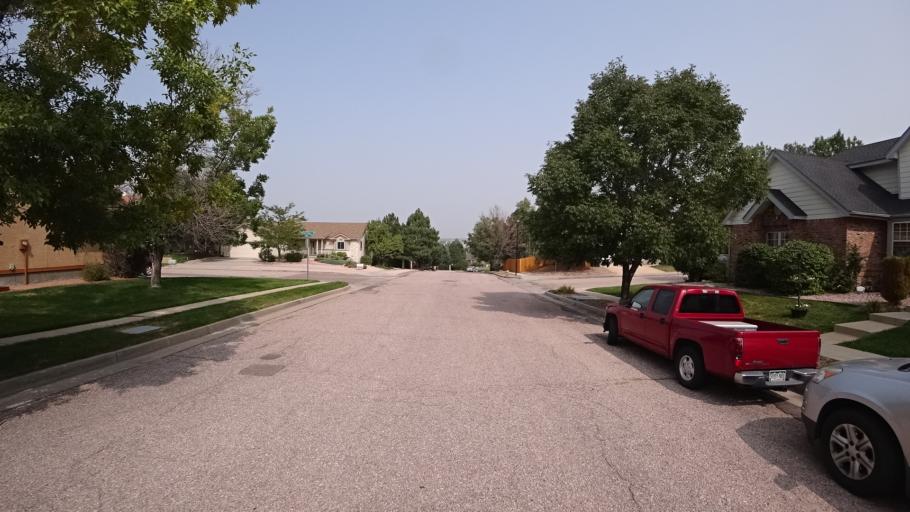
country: US
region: Colorado
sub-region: El Paso County
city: Cimarron Hills
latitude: 38.9194
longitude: -104.7428
